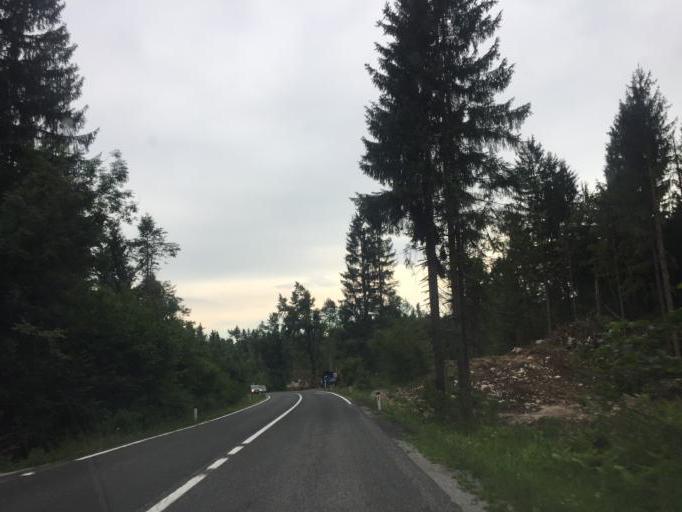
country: SI
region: Logatec
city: Logatec
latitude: 45.9098
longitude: 14.1606
